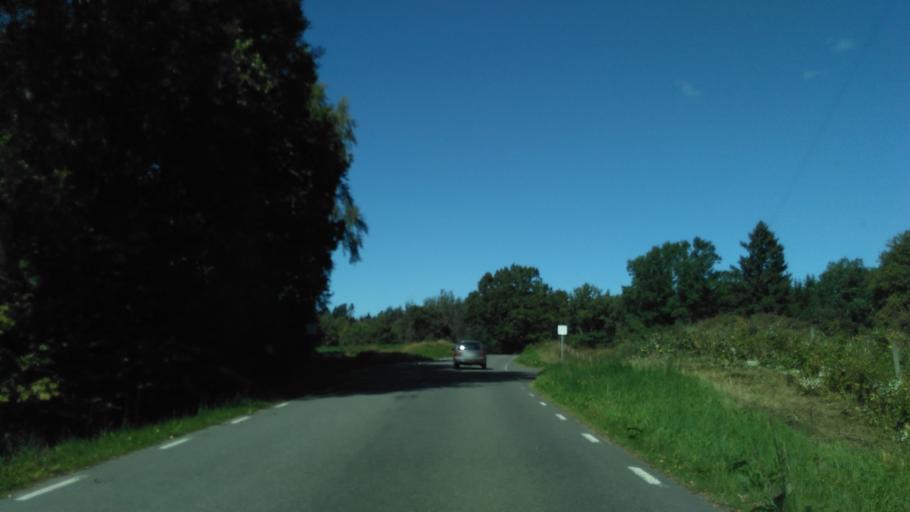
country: SE
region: Vaestra Goetaland
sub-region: Skara Kommun
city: Axvall
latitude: 58.4554
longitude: 13.6661
